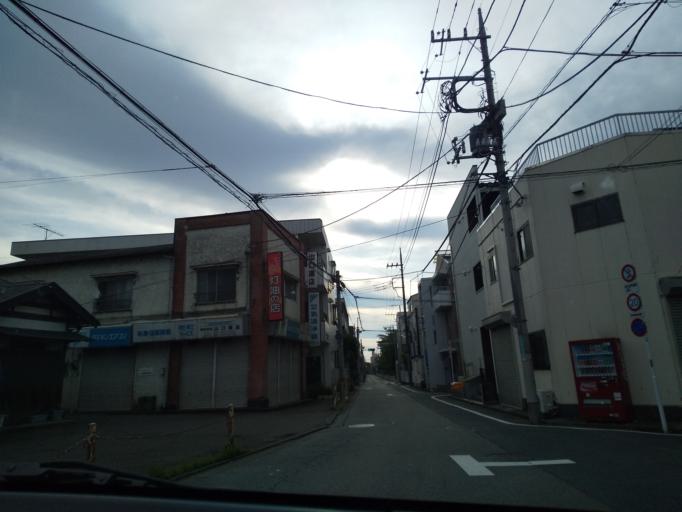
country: JP
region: Tokyo
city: Hino
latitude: 35.6935
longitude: 139.4305
